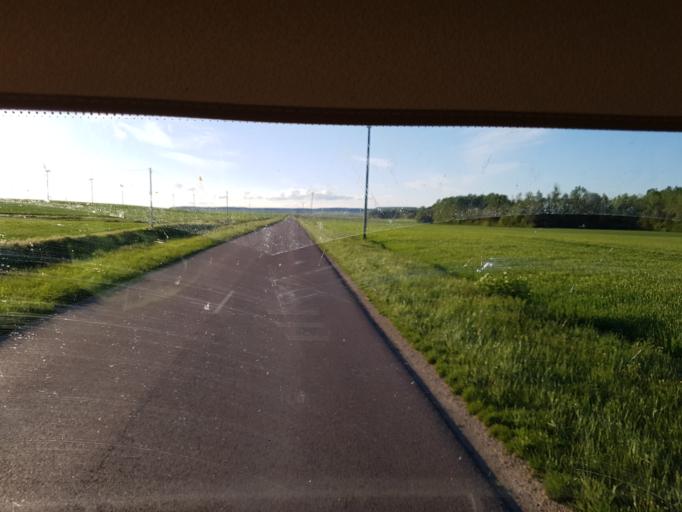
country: FR
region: Champagne-Ardenne
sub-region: Departement de l'Aube
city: Romilly-sur-Seine
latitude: 48.5602
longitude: 3.6654
